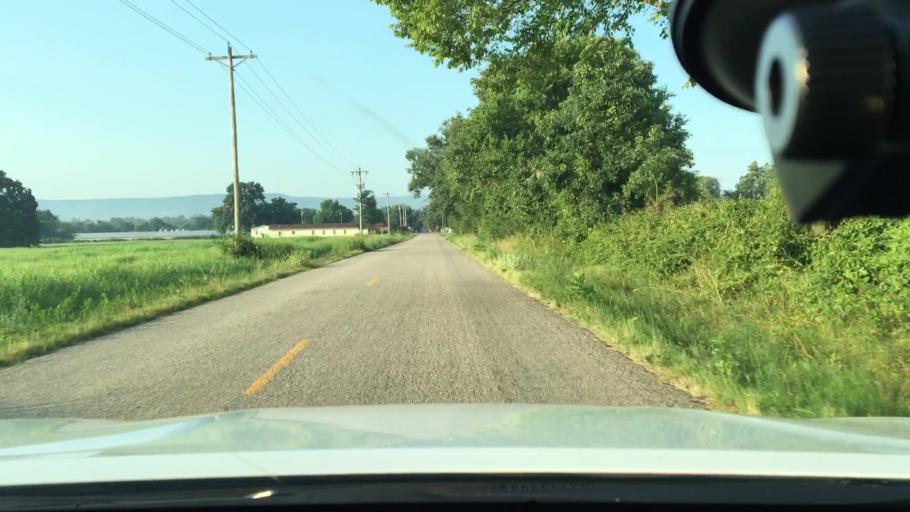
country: US
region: Arkansas
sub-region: Johnson County
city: Coal Hill
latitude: 35.3400
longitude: -93.6137
